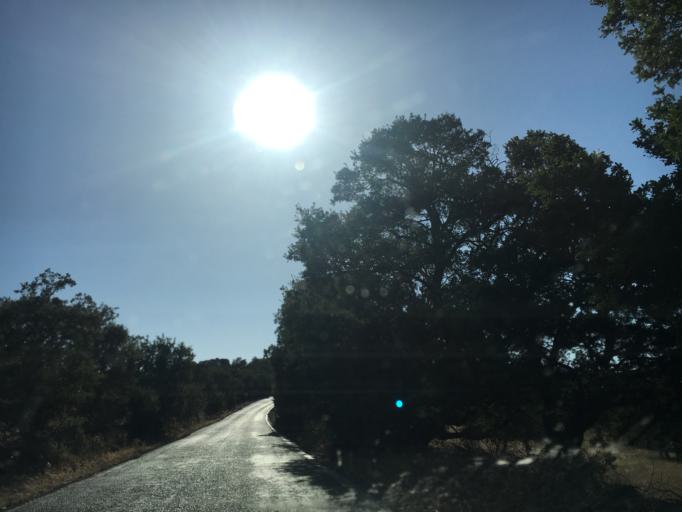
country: TR
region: Canakkale
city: Behram
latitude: 39.5023
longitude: 26.2791
